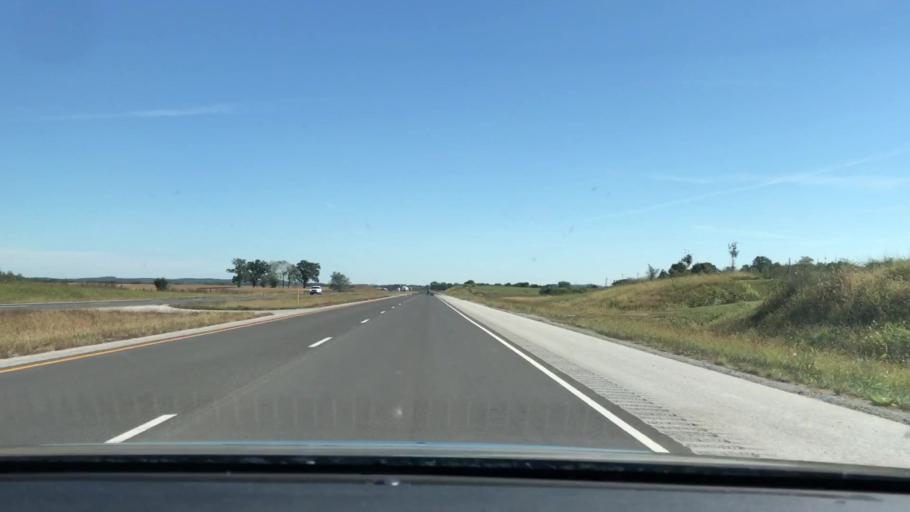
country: US
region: Kentucky
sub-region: Todd County
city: Elkton
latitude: 36.8083
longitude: -87.0458
